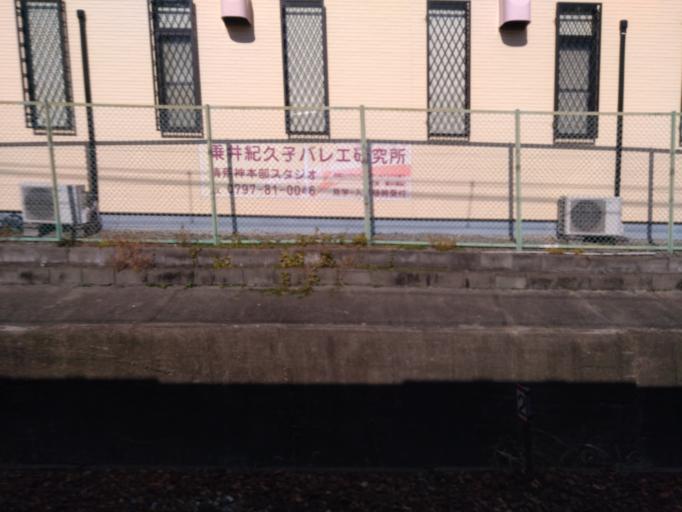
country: JP
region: Hyogo
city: Takarazuka
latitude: 34.8112
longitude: 135.3524
